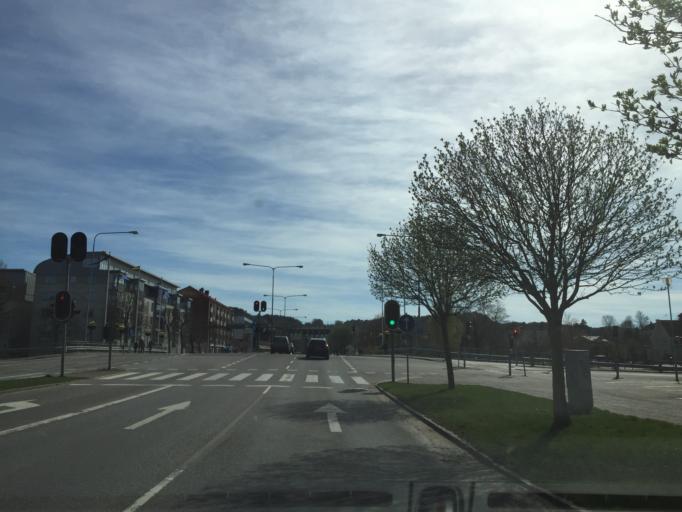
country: SE
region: Vaestra Goetaland
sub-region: Uddevalla Kommun
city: Uddevalla
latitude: 58.3495
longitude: 11.9318
